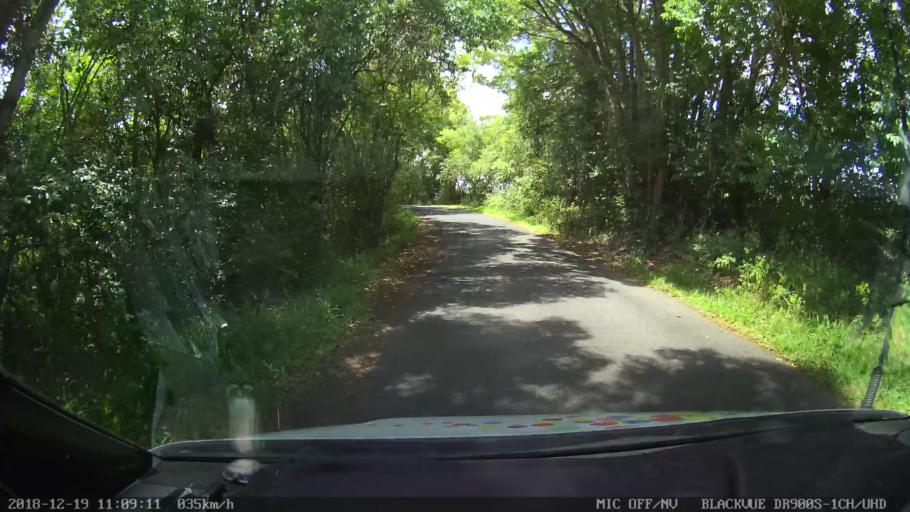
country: AU
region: New South Wales
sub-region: Lismore Municipality
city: Nimbin
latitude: -28.6332
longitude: 153.2639
